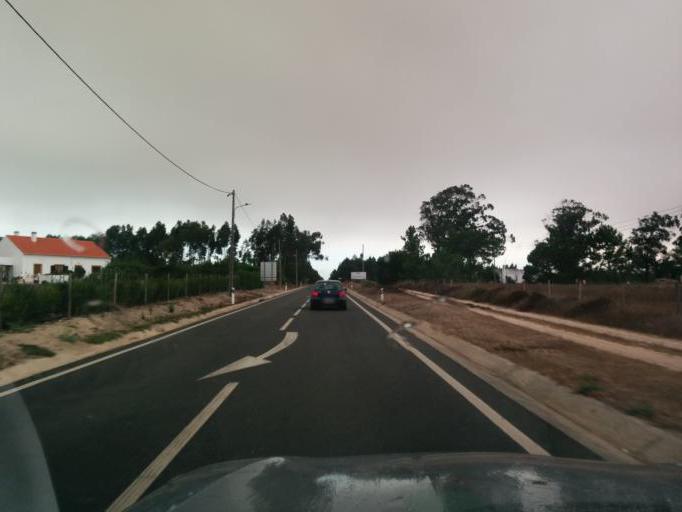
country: PT
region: Beja
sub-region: Odemira
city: Vila Nova de Milfontes
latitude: 37.6579
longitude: -8.7595
